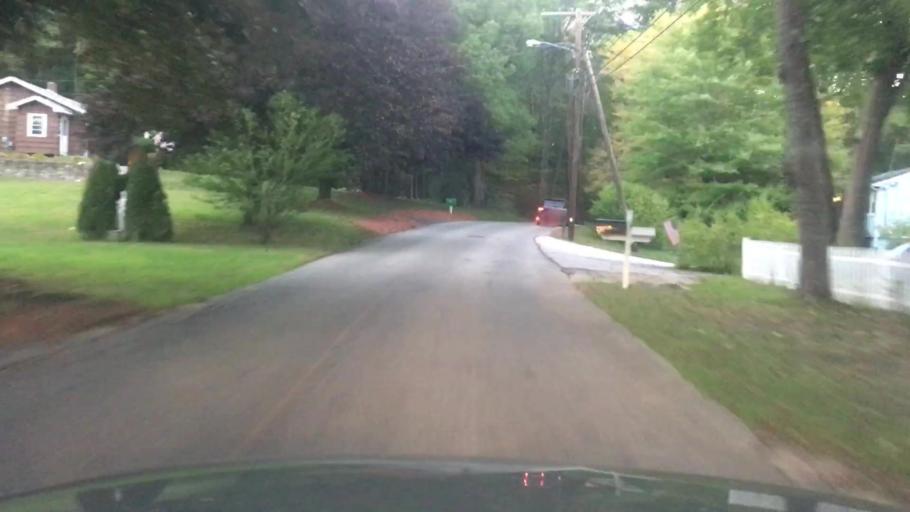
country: US
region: Massachusetts
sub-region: Worcester County
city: Charlton
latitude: 42.1297
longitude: -71.9753
